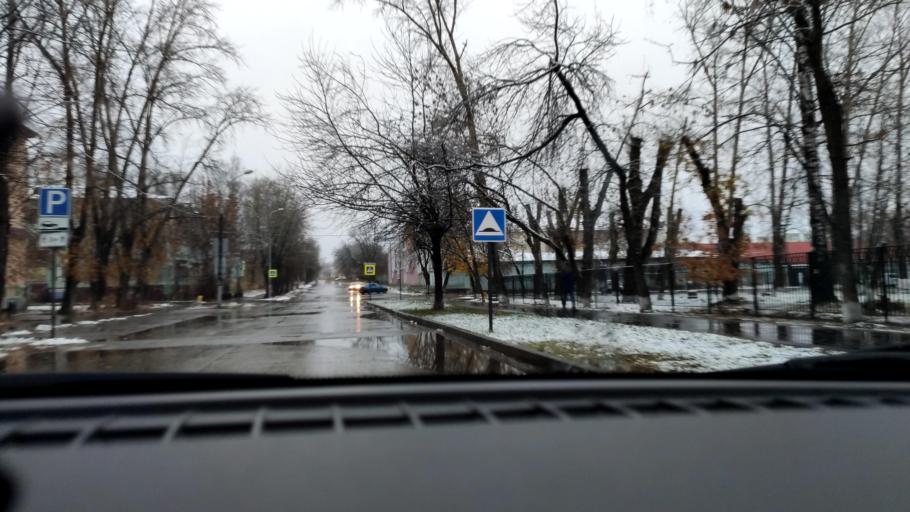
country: RU
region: Perm
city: Kultayevo
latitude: 57.9975
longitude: 55.9452
